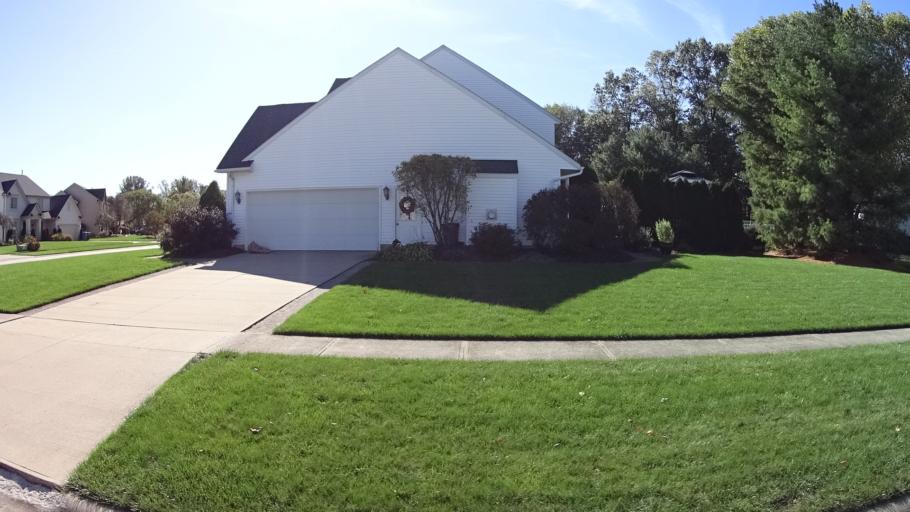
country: US
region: Ohio
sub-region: Lorain County
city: Amherst
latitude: 41.3952
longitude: -82.2438
